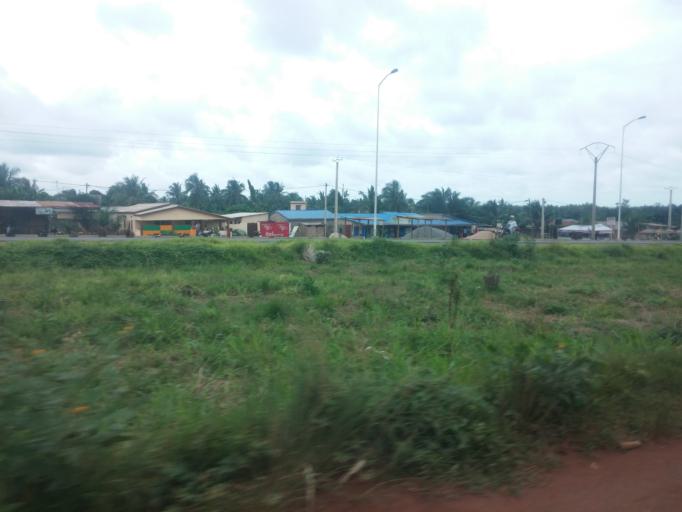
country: TG
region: Maritime
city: Tsevie
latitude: 6.3179
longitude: 1.2174
